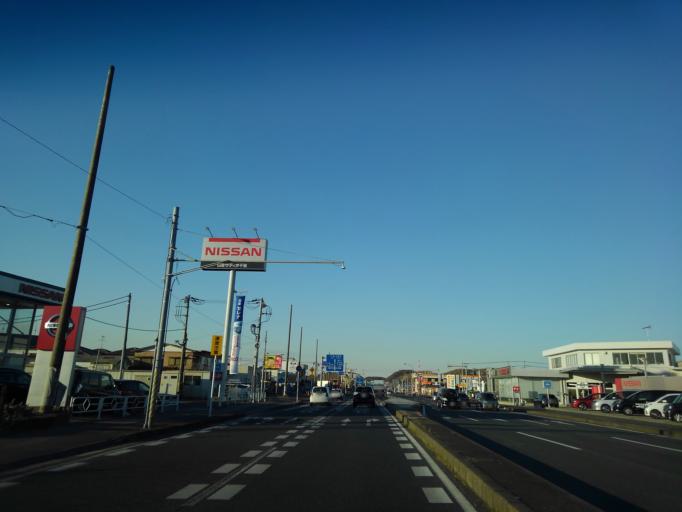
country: JP
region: Chiba
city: Kimitsu
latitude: 35.3168
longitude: 139.9269
